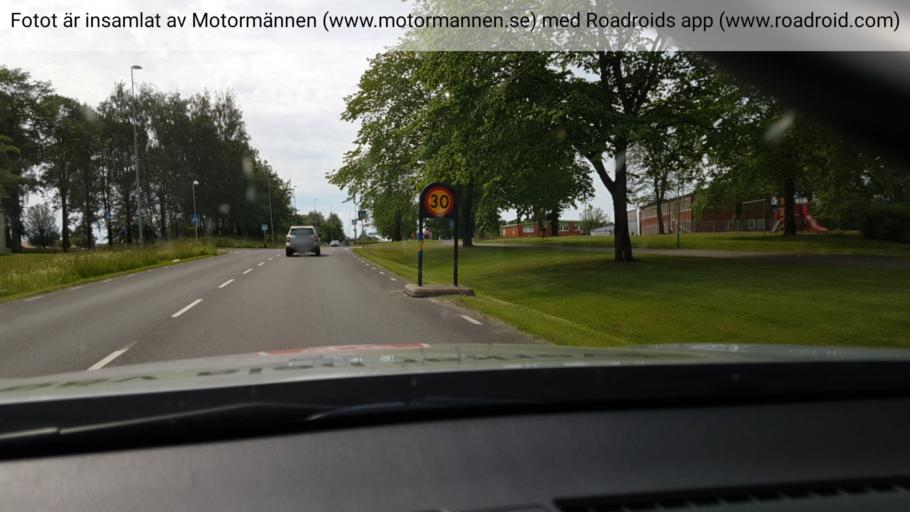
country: SE
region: Vaestra Goetaland
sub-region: Falkopings Kommun
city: Falkoeping
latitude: 58.1682
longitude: 13.5690
